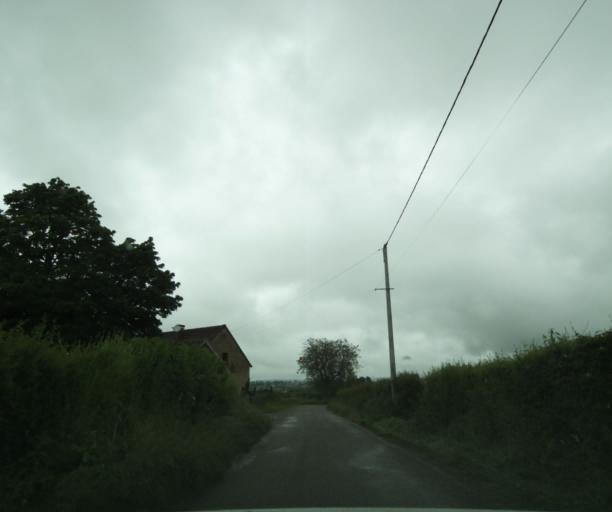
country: FR
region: Bourgogne
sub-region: Departement de Saone-et-Loire
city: Charolles
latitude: 46.4301
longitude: 4.3500
